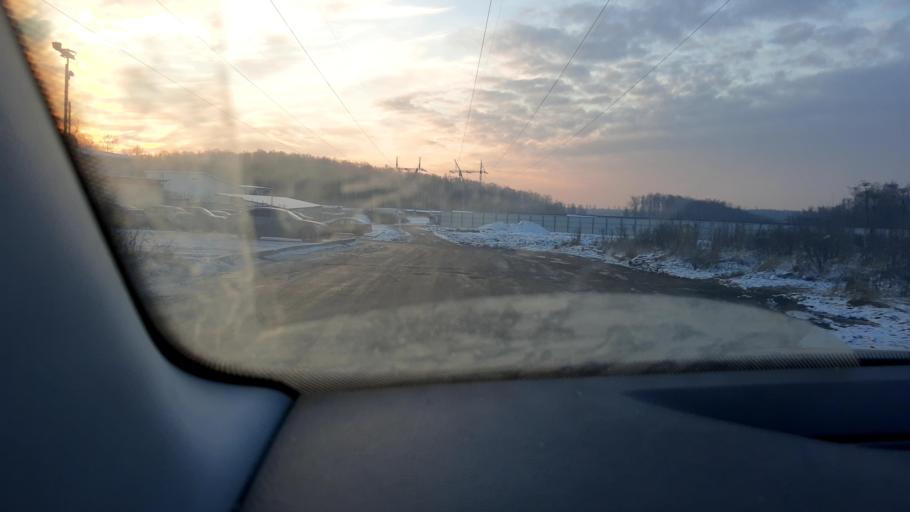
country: RU
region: Moscow
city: Zagor'ye
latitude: 55.5630
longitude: 37.6496
